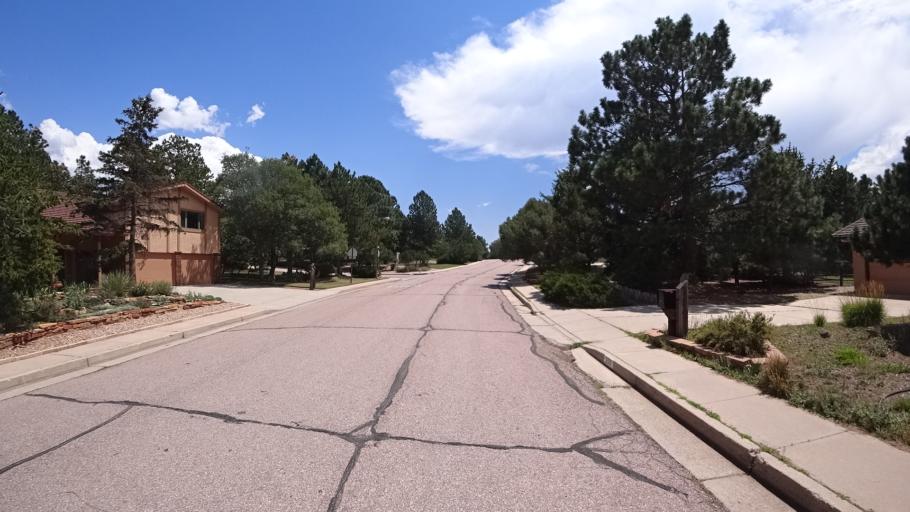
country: US
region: Colorado
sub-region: El Paso County
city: Air Force Academy
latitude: 38.9350
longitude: -104.8325
